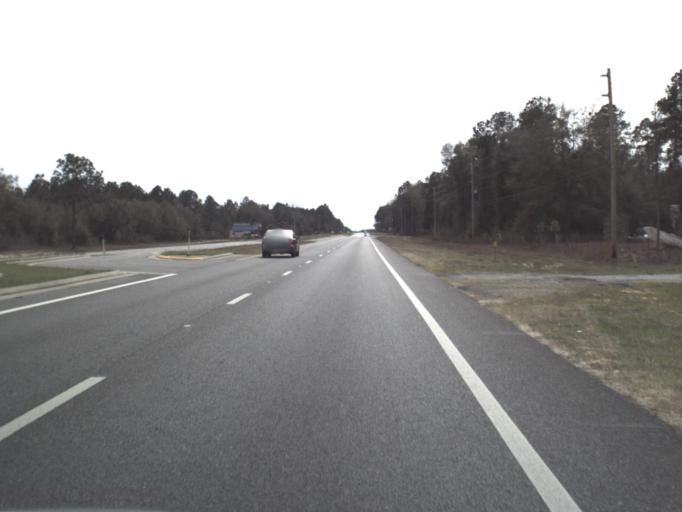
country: US
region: Florida
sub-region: Bay County
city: Youngstown
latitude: 30.5190
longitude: -85.4088
